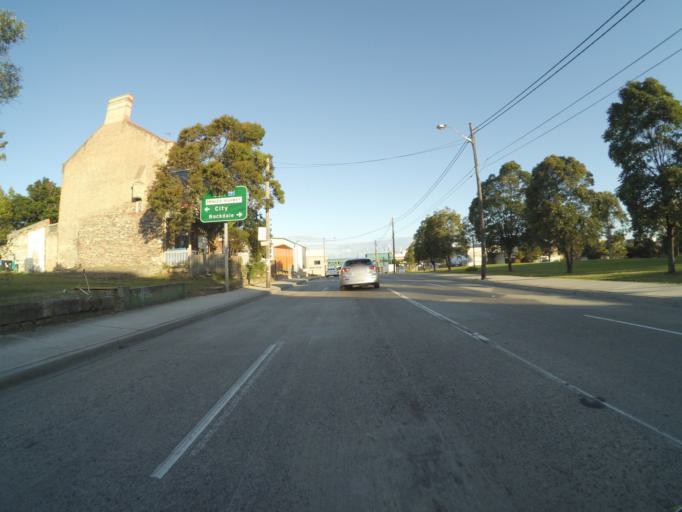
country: AU
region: New South Wales
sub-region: Marrickville
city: Newtown
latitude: -33.9182
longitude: 151.1683
